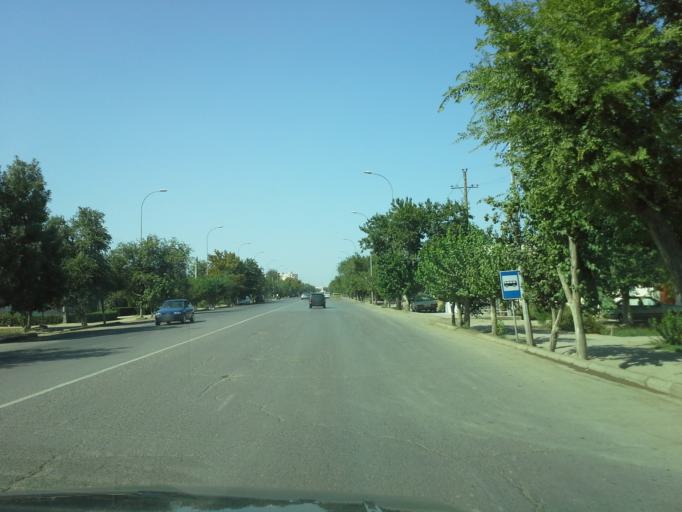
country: TM
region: Dasoguz
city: Dasoguz
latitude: 41.8242
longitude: 59.9766
